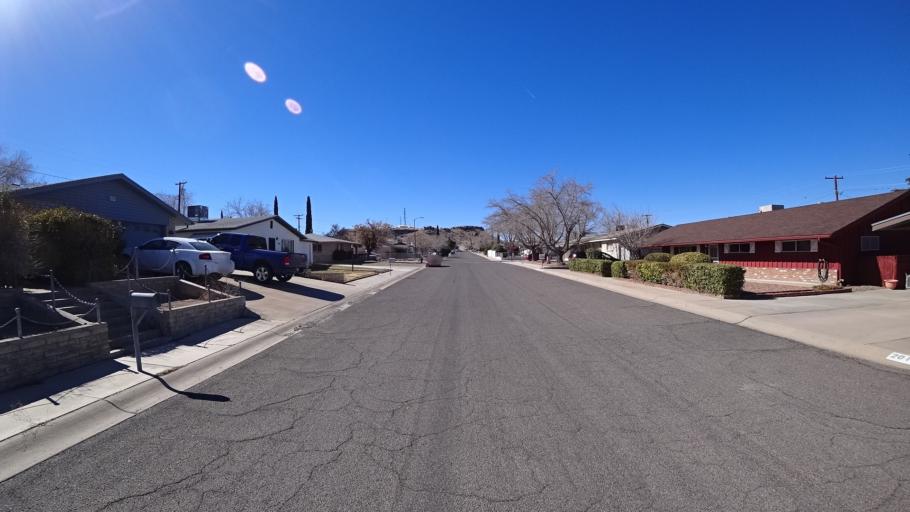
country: US
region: Arizona
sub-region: Mohave County
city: Kingman
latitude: 35.1987
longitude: -114.0306
